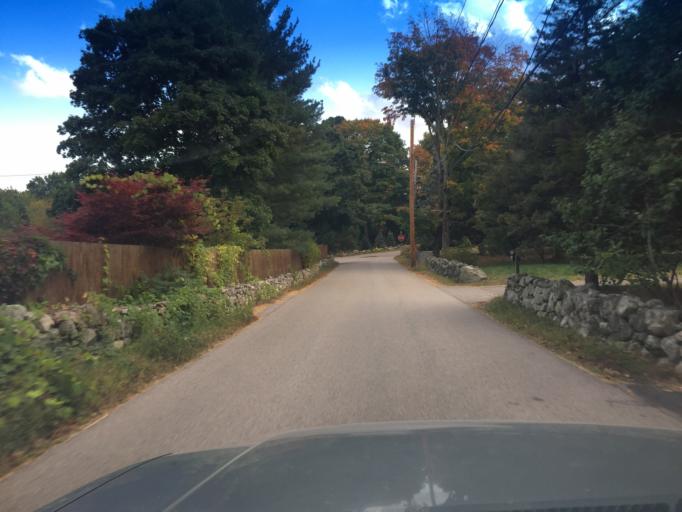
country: US
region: Massachusetts
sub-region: Norfolk County
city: Westwood
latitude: 42.2152
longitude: -71.2111
